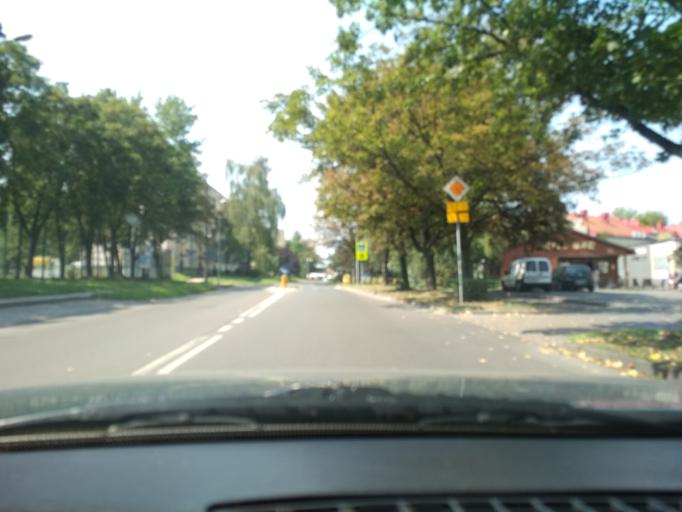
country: PL
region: Silesian Voivodeship
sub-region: Siemianowice Slaskie
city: Siemianowice Slaskie
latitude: 50.3023
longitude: 19.0079
